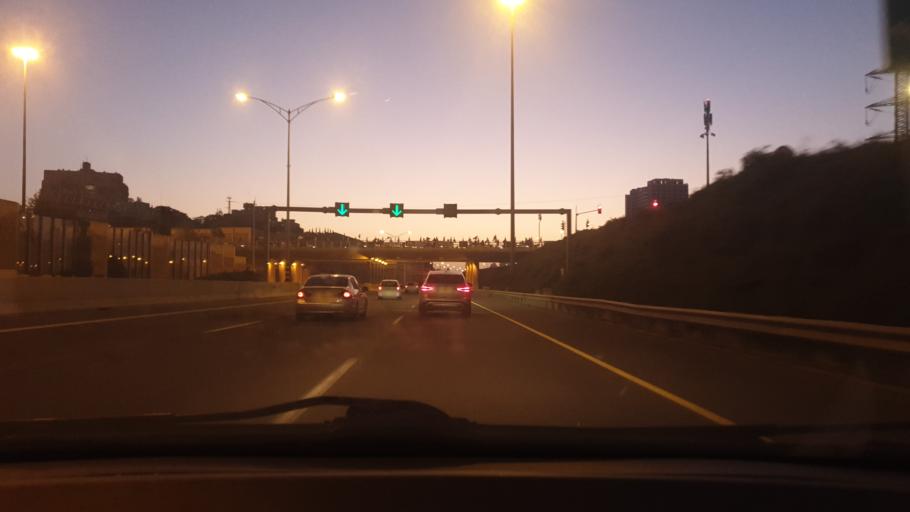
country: IL
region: Central District
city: Ganne Tiqwa
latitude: 32.0695
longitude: 34.8614
